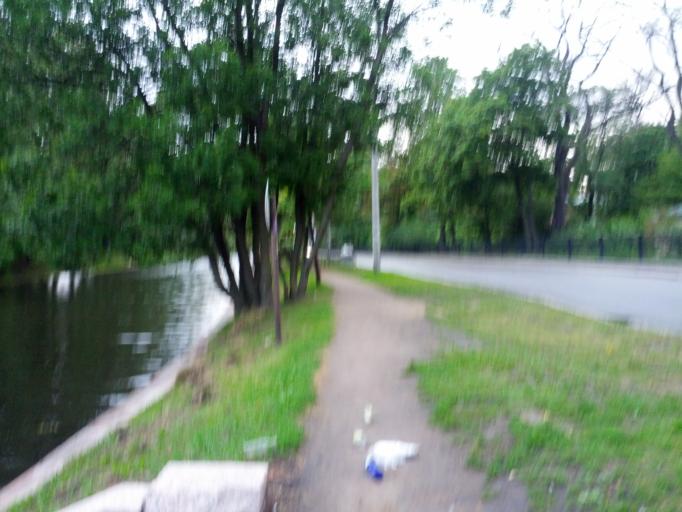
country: RU
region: St.-Petersburg
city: Petrogradka
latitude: 59.9685
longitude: 30.3251
